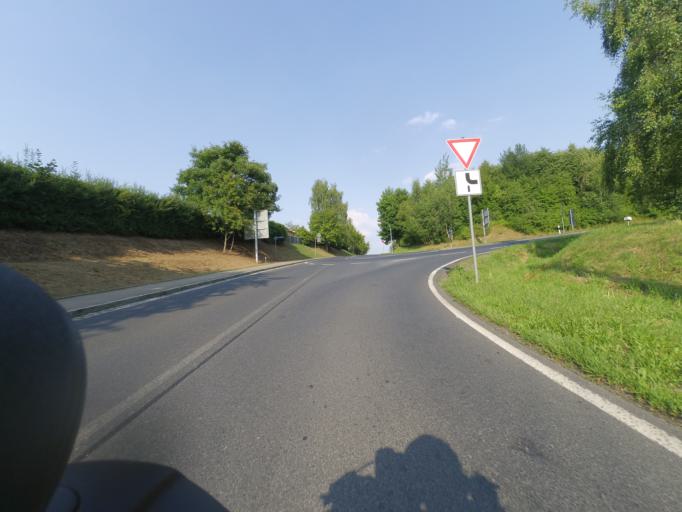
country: DE
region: Saxony
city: Nossen
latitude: 51.0581
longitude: 13.2824
